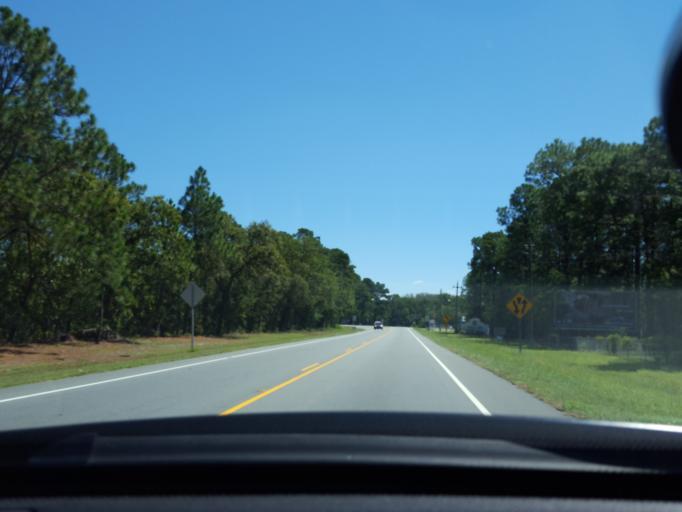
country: US
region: North Carolina
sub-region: Bladen County
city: Elizabethtown
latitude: 34.6488
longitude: -78.5311
